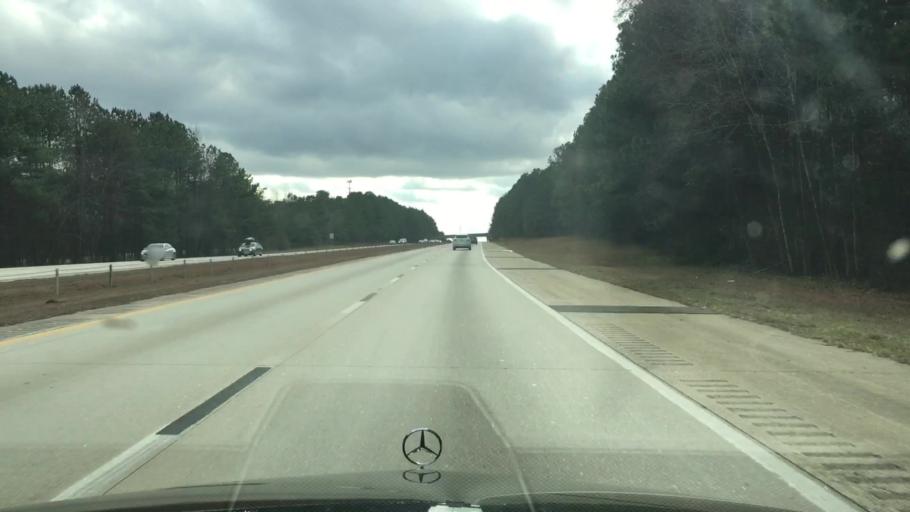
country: US
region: North Carolina
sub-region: Wake County
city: Garner
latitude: 35.6715
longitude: -78.5635
